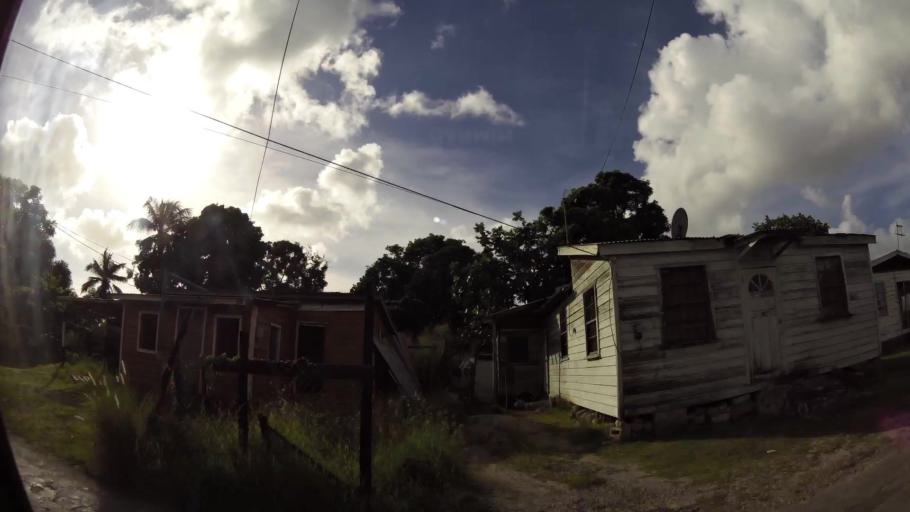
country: BB
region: Saint Michael
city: Bridgetown
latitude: 13.0905
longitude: -59.5886
